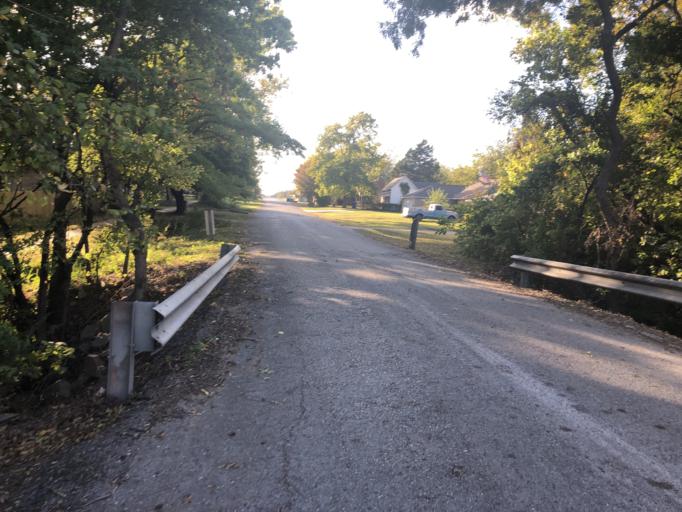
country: US
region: Oklahoma
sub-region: Pottawatomie County
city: Tecumseh
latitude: 35.2587
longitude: -96.9328
